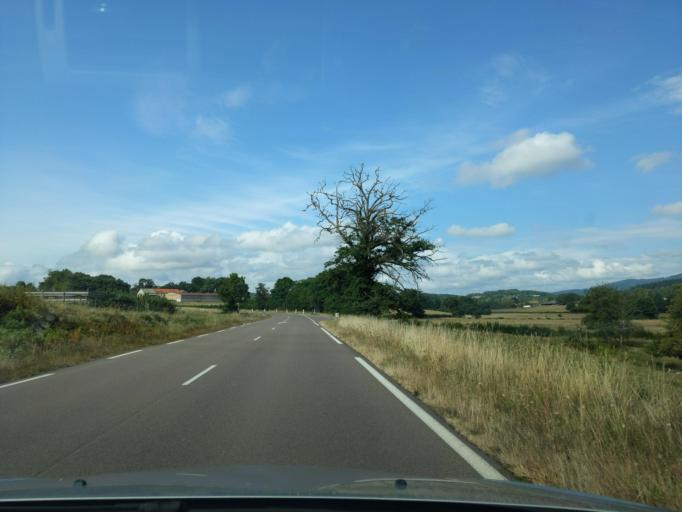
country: FR
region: Bourgogne
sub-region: Departement de Saone-et-Loire
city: Etang-sur-Arroux
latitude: 46.8983
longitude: 4.1594
